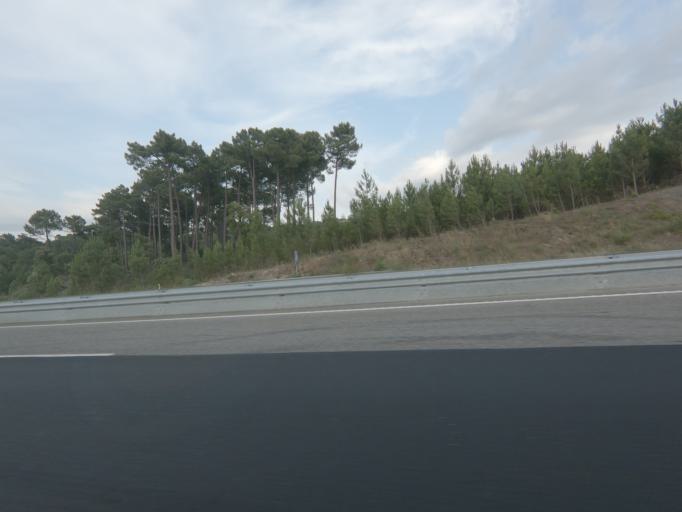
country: PT
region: Vila Real
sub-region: Boticas
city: Boticas
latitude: 41.6188
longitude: -7.6055
